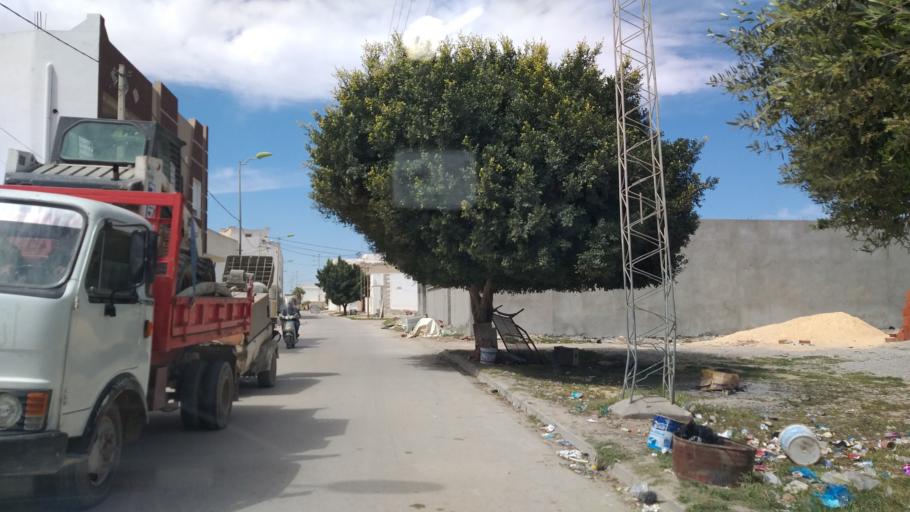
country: TN
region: Al Mahdiyah
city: El Jem
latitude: 35.2999
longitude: 10.7031
